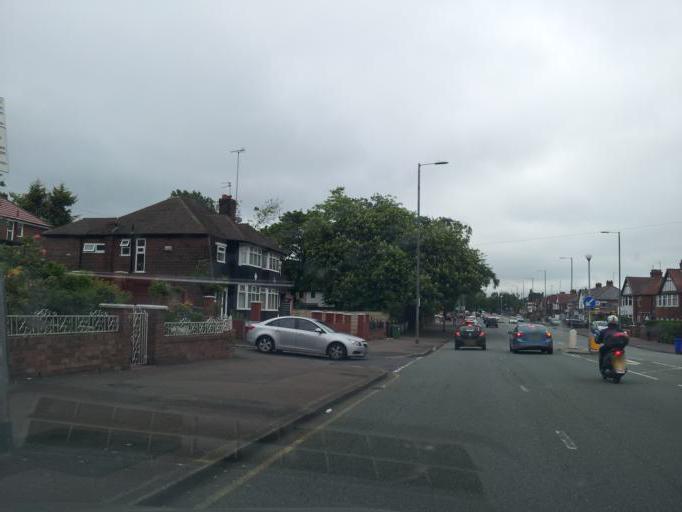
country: GB
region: England
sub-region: Manchester
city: Crumpsall
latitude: 53.5266
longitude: -2.2477
